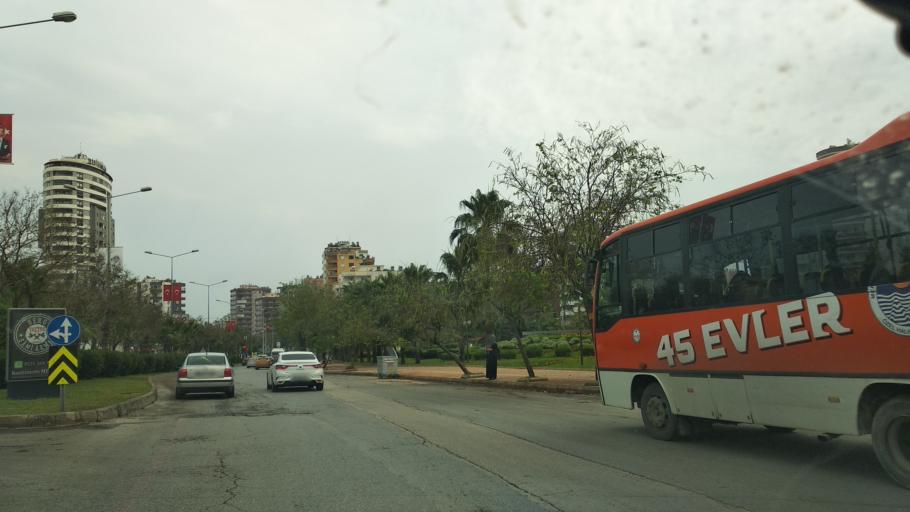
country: TR
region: Mersin
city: Mercin
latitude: 36.8001
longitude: 34.5943
